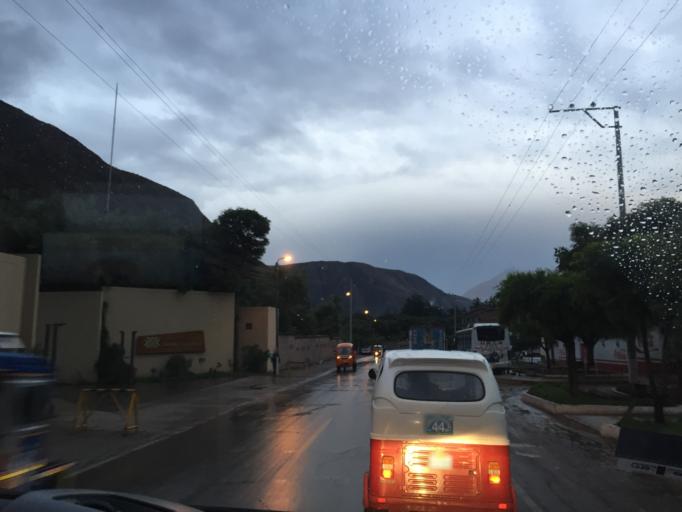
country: PE
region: Cusco
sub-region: Provincia de Urubamba
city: Urubamba
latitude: -13.3088
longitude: -72.1171
